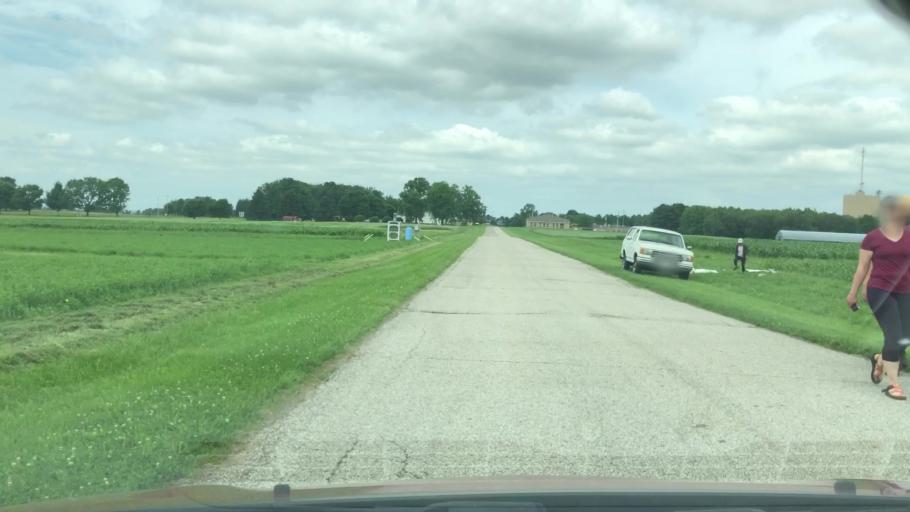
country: US
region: Ohio
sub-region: Wayne County
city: Wooster
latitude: 40.7713
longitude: -81.9059
